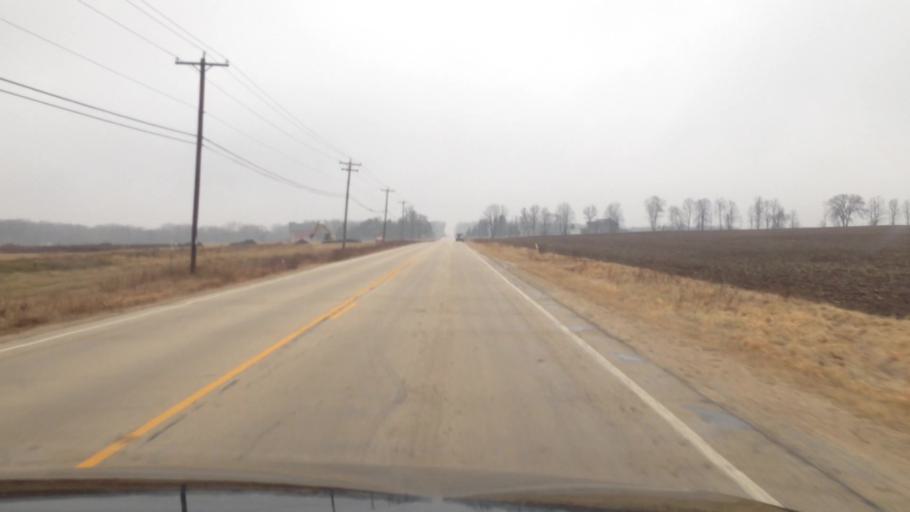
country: US
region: Wisconsin
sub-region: Washington County
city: Richfield
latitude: 43.2536
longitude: -88.1625
